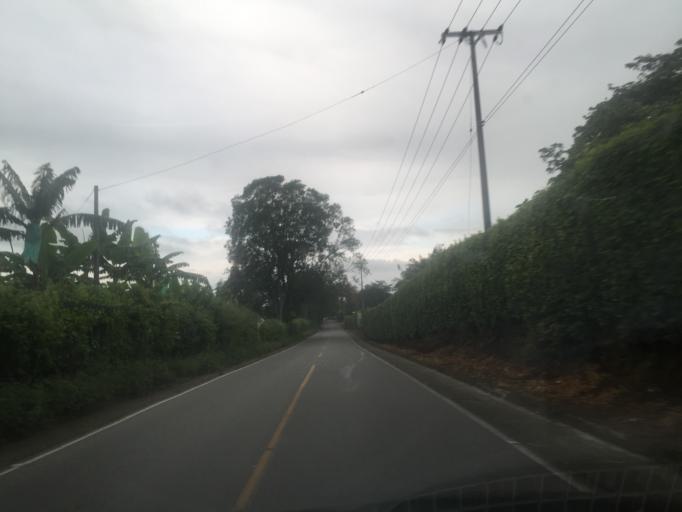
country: CO
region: Quindio
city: Armenia
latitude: 4.5150
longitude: -75.7235
